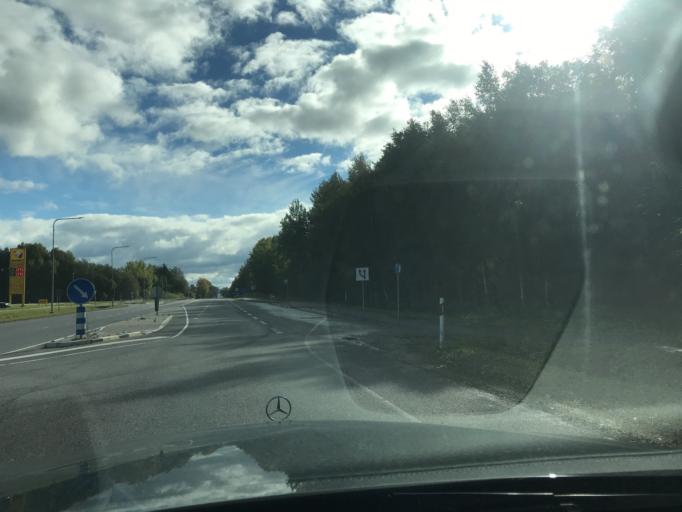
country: EE
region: Vorumaa
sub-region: Voru linn
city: Voru
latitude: 57.8586
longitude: 26.9741
